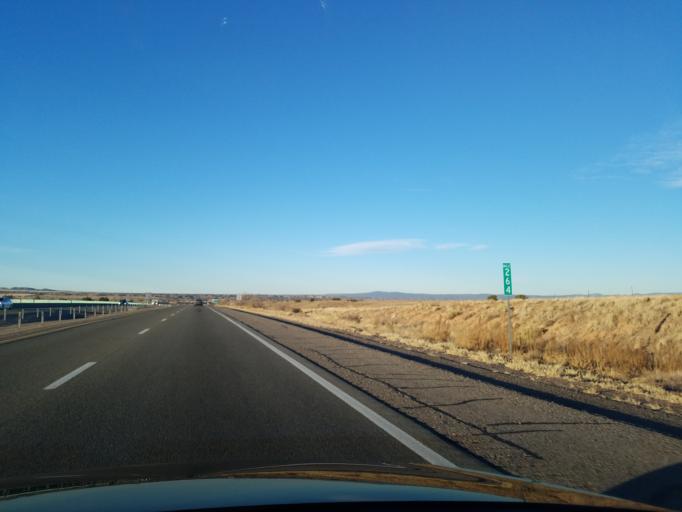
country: US
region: New Mexico
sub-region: Santa Fe County
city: La Cienega
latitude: 35.5114
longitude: -106.2356
